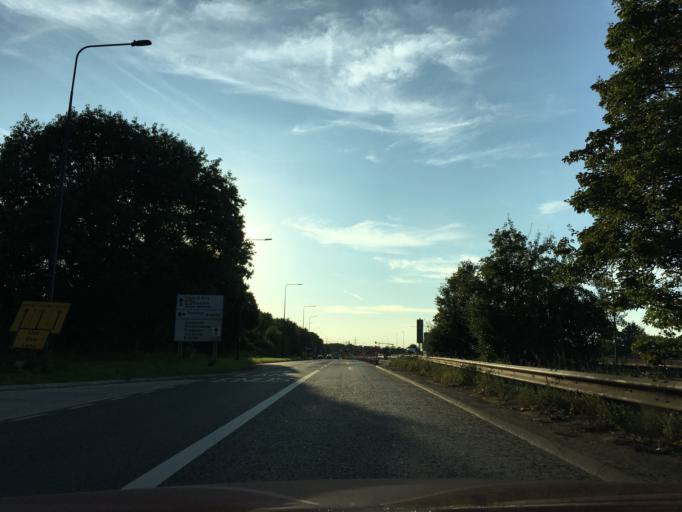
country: GB
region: England
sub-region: South Gloucestershire
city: Mangotsfield
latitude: 51.5034
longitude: -2.5170
